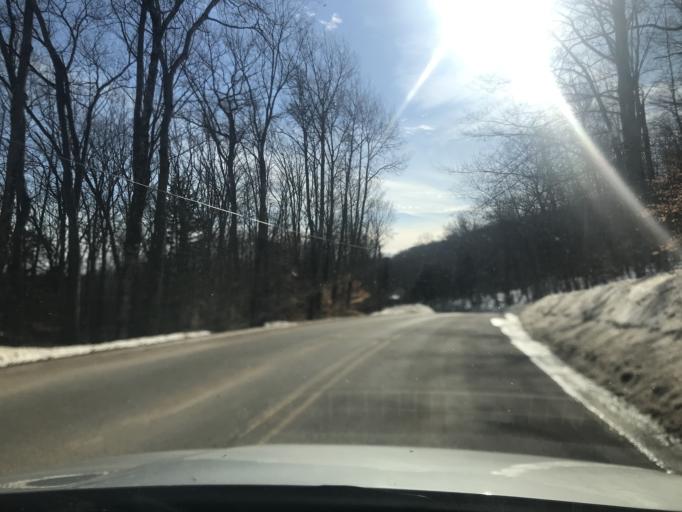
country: US
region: Michigan
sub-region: Dickinson County
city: Kingsford
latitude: 45.4052
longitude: -88.3473
